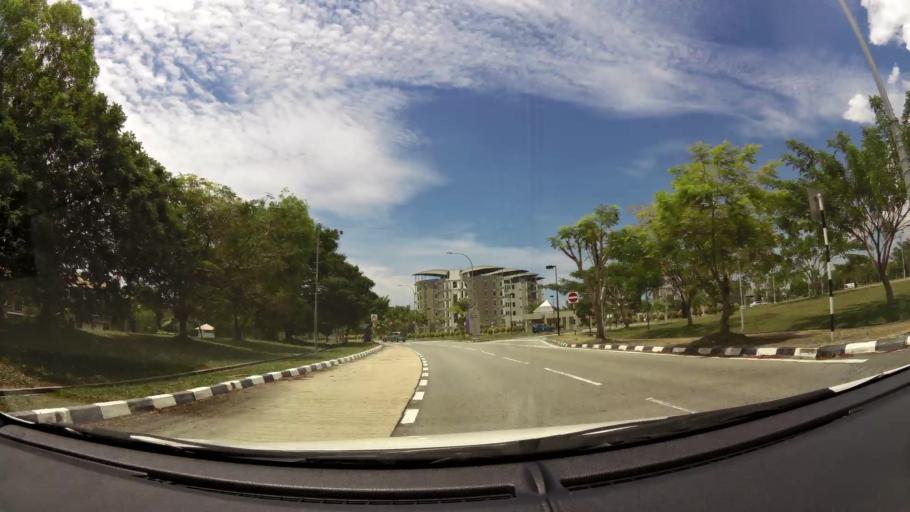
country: BN
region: Brunei and Muara
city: Bandar Seri Begawan
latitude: 4.9789
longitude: 114.8965
